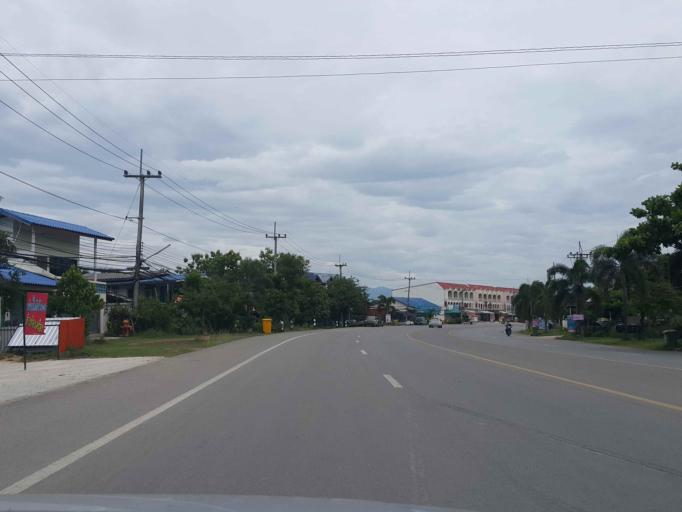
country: TH
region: Lampang
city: Thoen
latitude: 17.6325
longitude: 99.2364
